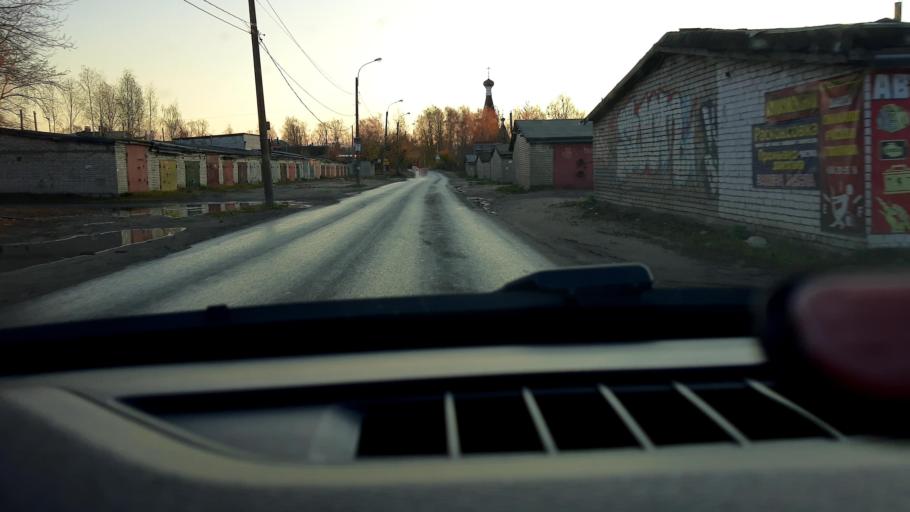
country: RU
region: Nizjnij Novgorod
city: Gorbatovka
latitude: 56.3309
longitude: 43.8185
